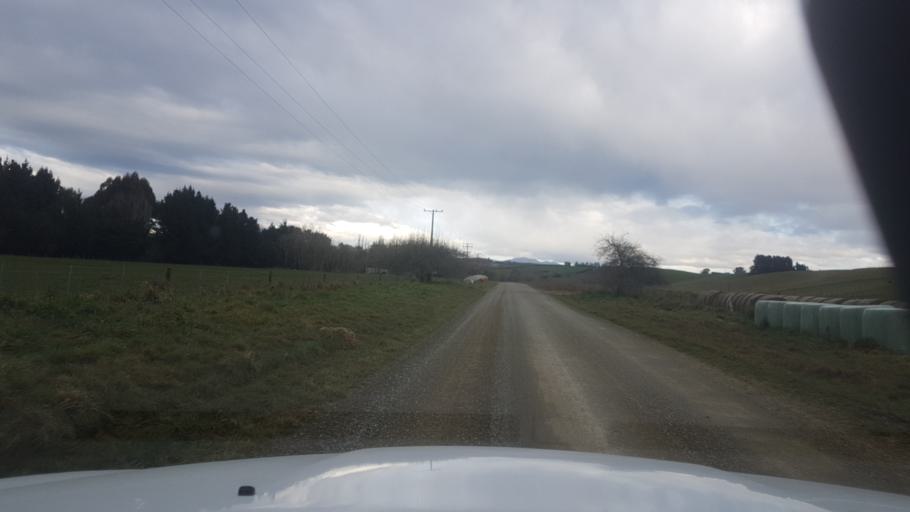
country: NZ
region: Canterbury
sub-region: Timaru District
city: Pleasant Point
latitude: -44.3388
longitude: 171.1762
